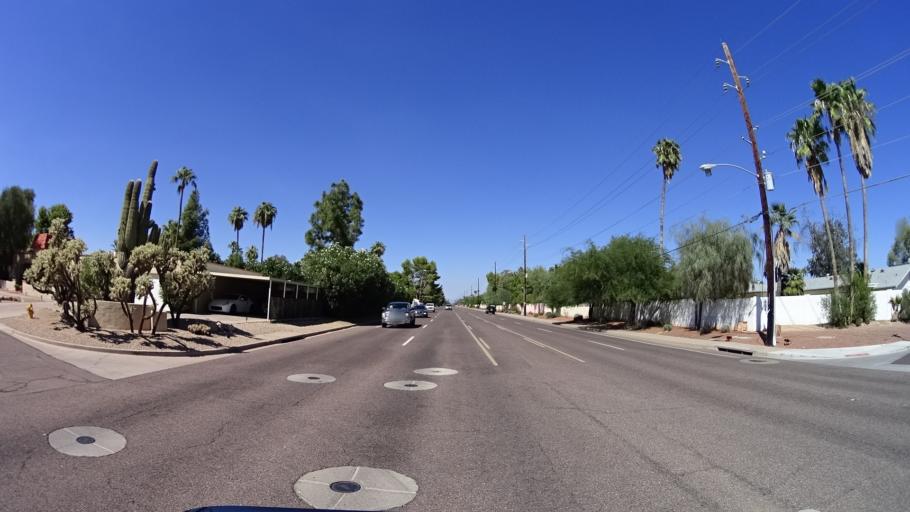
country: US
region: Arizona
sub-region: Maricopa County
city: Paradise Valley
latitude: 33.6009
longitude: -111.9606
